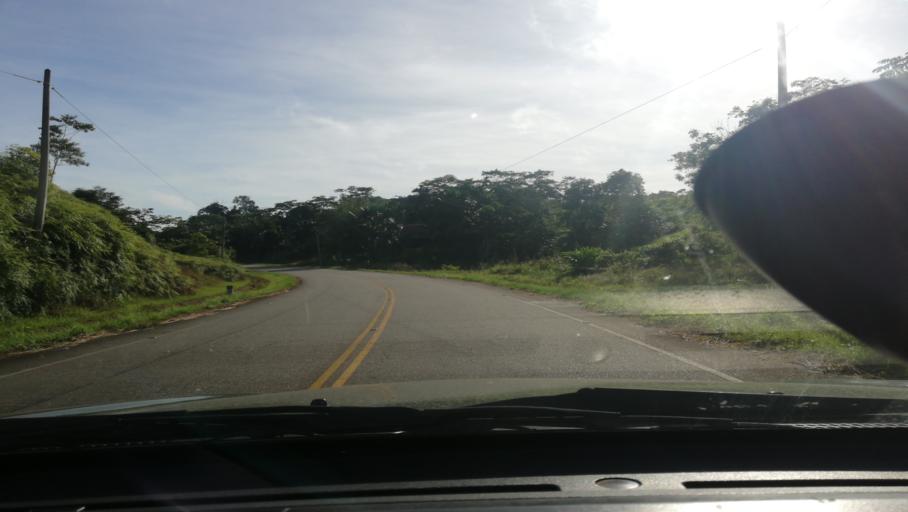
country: PE
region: Loreto
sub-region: Provincia de Loreto
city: Nauta
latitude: -4.4035
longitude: -73.5760
